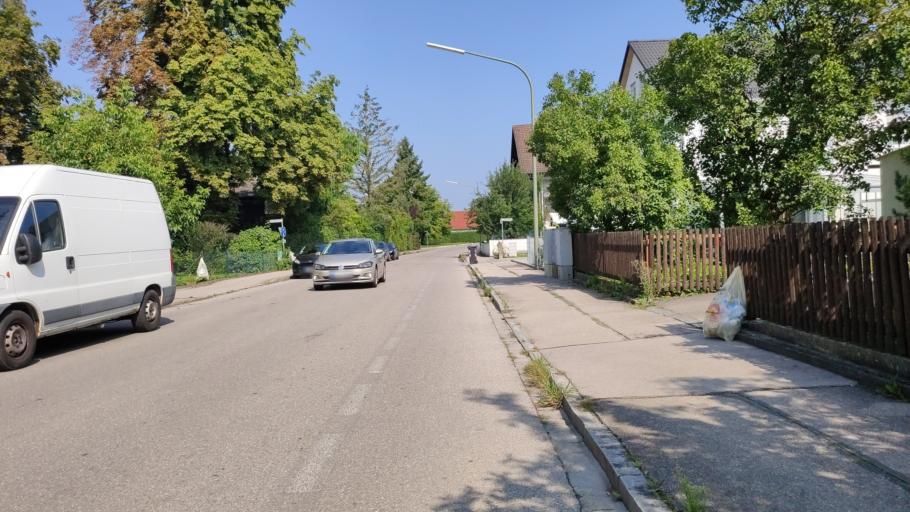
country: DE
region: Bavaria
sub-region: Swabia
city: Schwabmunchen
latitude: 48.1873
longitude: 10.7566
